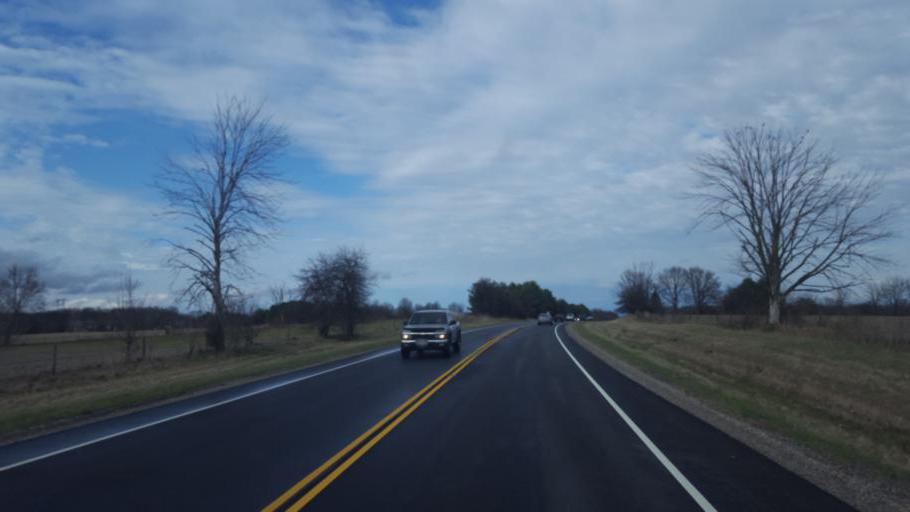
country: US
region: Ohio
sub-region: Delaware County
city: Sunbury
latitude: 40.2114
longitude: -82.9028
